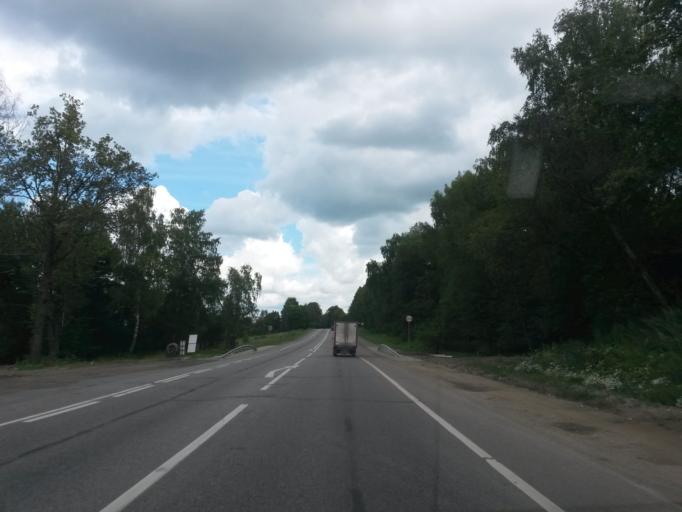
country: RU
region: Vladimir
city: Strunino
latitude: 56.5672
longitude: 38.5879
